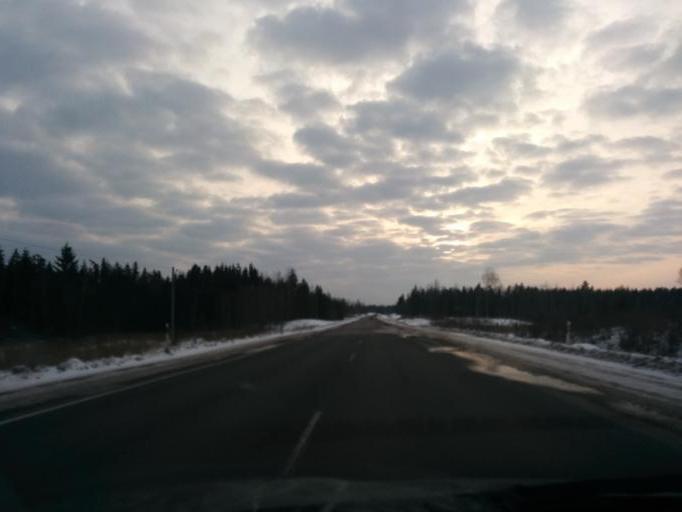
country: LV
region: Smiltene
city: Smiltene
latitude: 57.3342
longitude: 25.8196
